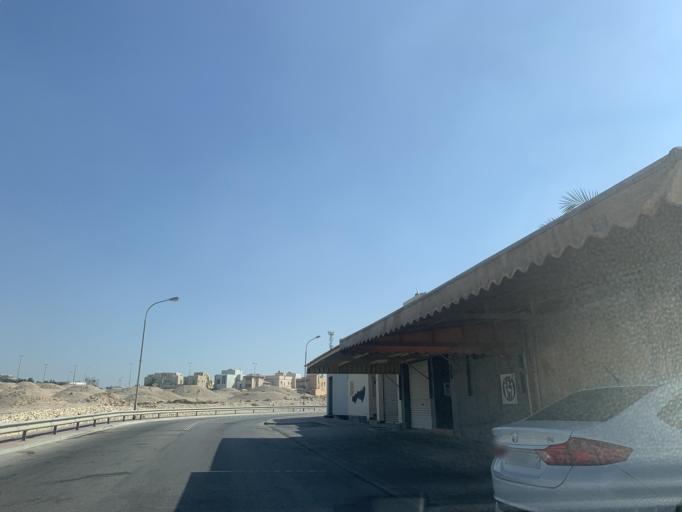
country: BH
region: Central Governorate
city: Madinat Hamad
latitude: 26.1172
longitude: 50.4990
